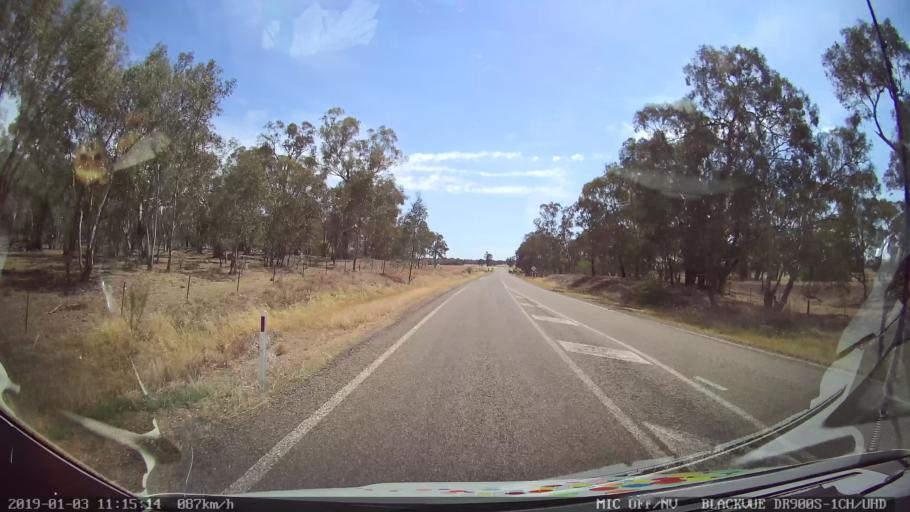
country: AU
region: New South Wales
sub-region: Young
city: Young
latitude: -34.1661
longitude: 148.2630
